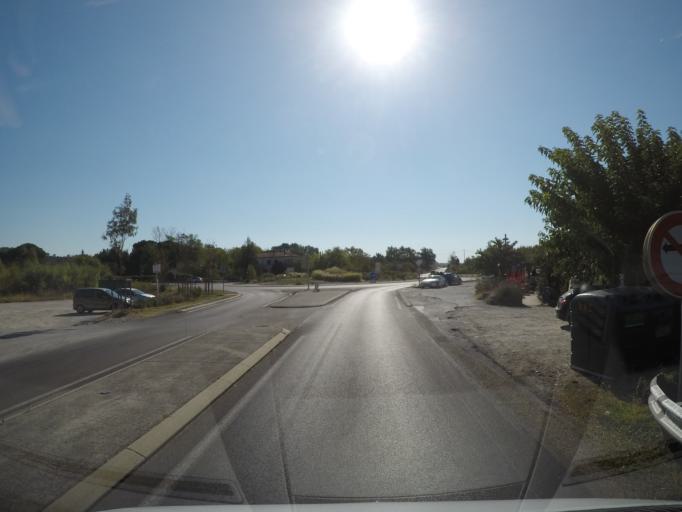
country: FR
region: Languedoc-Roussillon
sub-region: Departement du Gard
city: Ribaute-les-Tavernes
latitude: 44.0202
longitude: 4.1018
